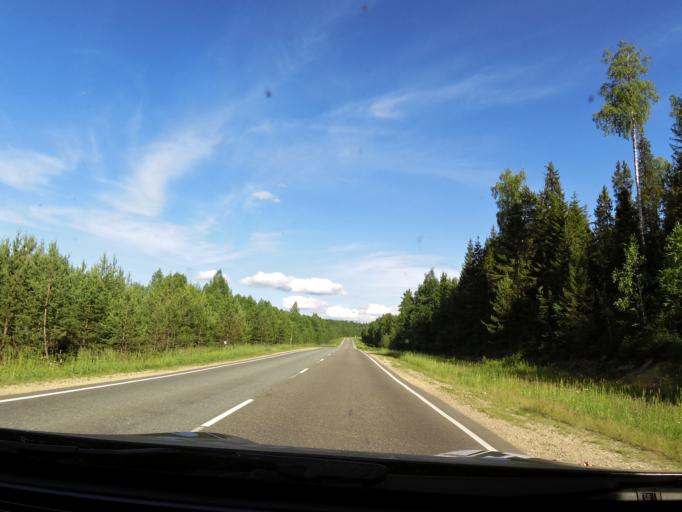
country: RU
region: Kirov
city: Chernaya Kholunitsa
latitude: 58.8237
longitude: 51.7950
